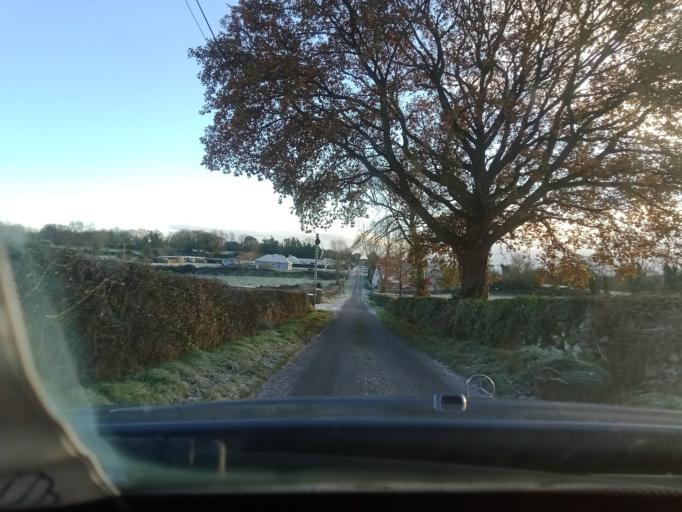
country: IE
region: Leinster
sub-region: Kilkenny
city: Graiguenamanagh
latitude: 52.5988
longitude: -6.9714
